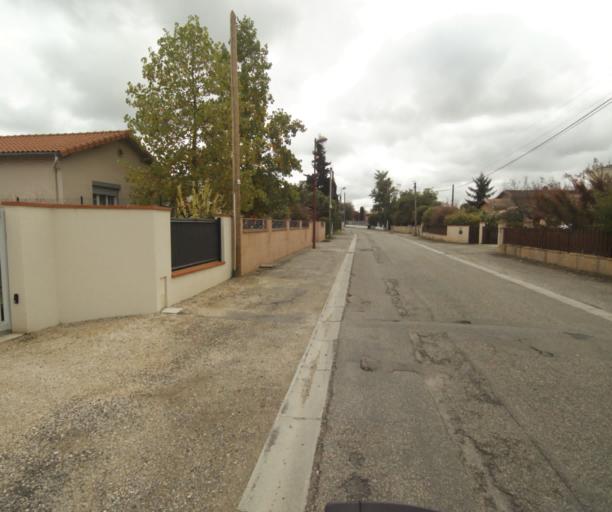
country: FR
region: Midi-Pyrenees
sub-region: Departement du Tarn-et-Garonne
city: Montech
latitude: 43.9551
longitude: 1.2343
